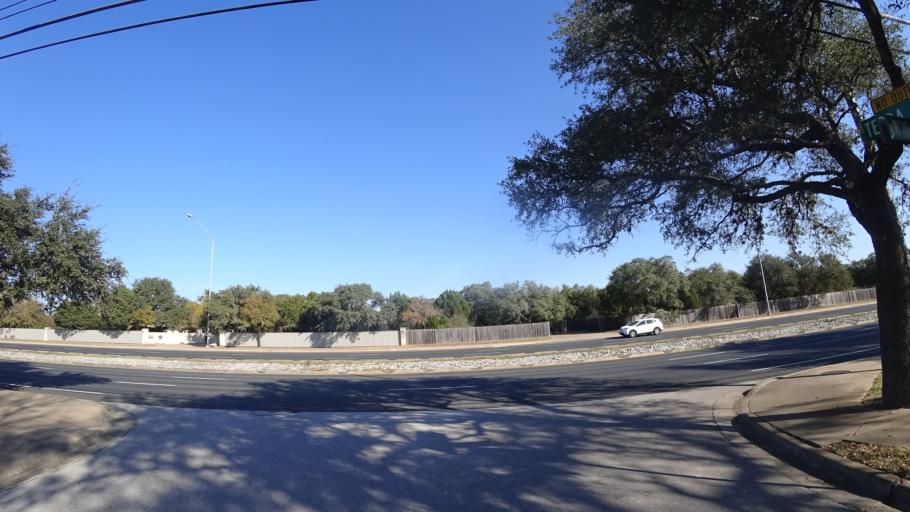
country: US
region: Texas
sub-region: Travis County
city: Shady Hollow
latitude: 30.2243
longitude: -97.8475
